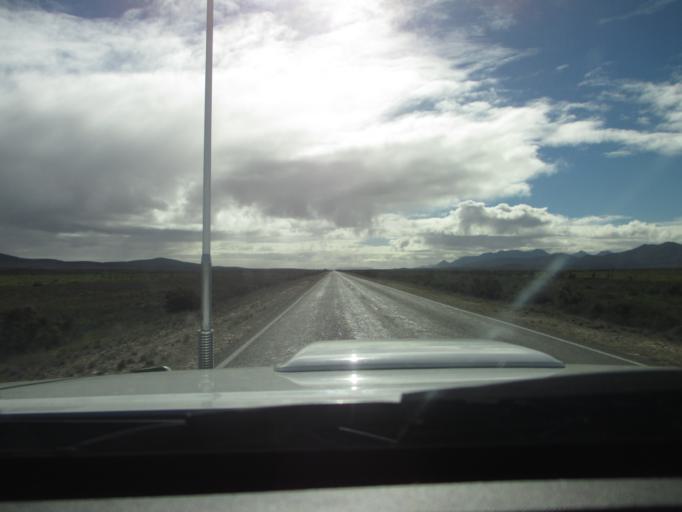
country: AU
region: South Australia
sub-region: Flinders Ranges
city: Quorn
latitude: -31.6773
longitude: 138.3676
